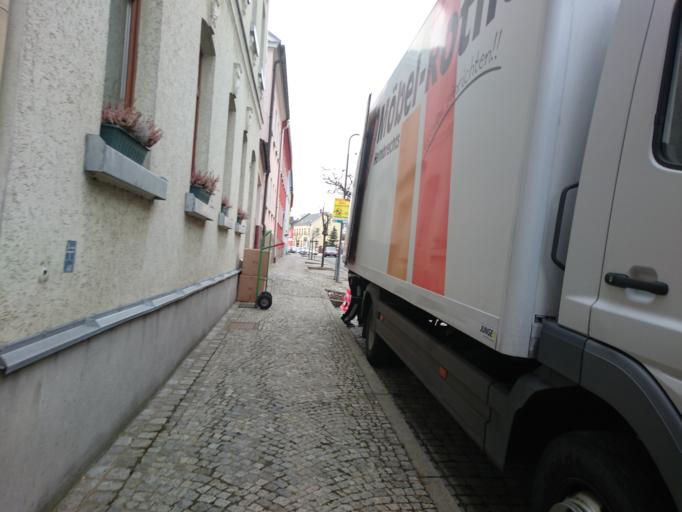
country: DE
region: Thuringia
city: Tanna
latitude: 50.4943
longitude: 11.8624
